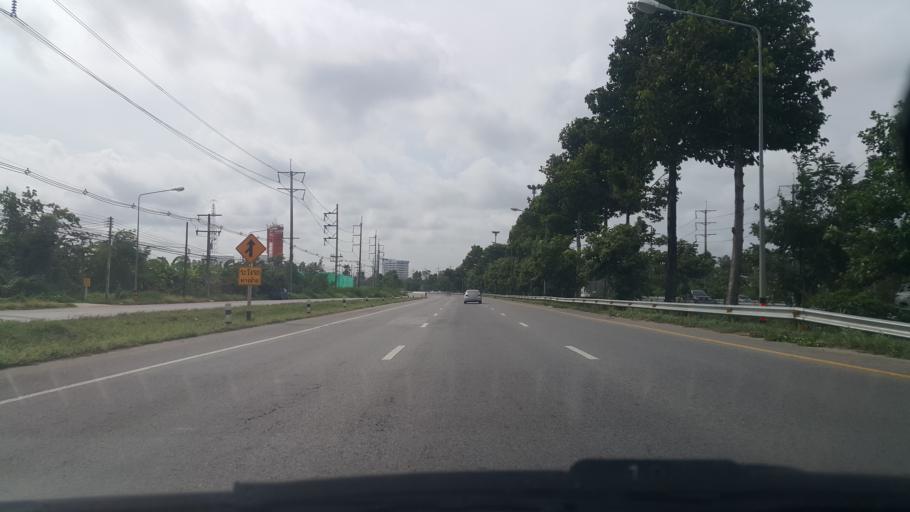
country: TH
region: Rayong
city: Rayong
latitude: 12.6864
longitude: 101.2980
